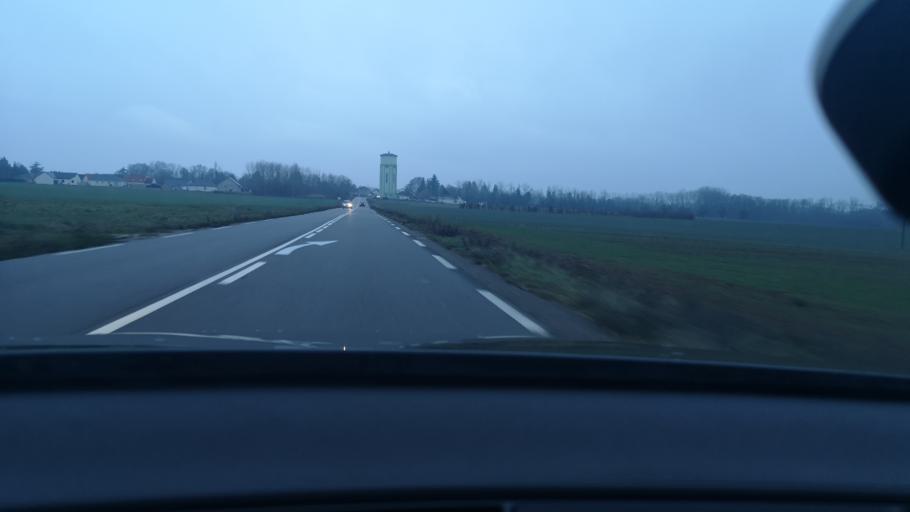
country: FR
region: Bourgogne
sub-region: Departement de la Cote-d'Or
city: Seurre
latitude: 47.0714
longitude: 5.1002
